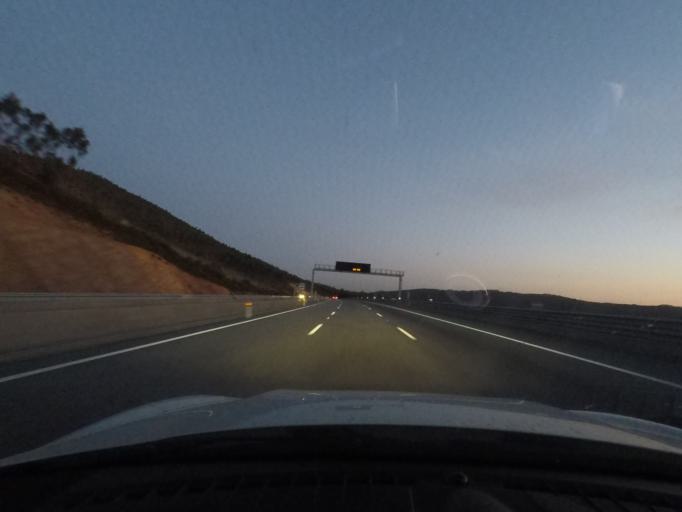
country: PT
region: Porto
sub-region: Paredes
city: Recarei
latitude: 41.1186
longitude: -8.4334
